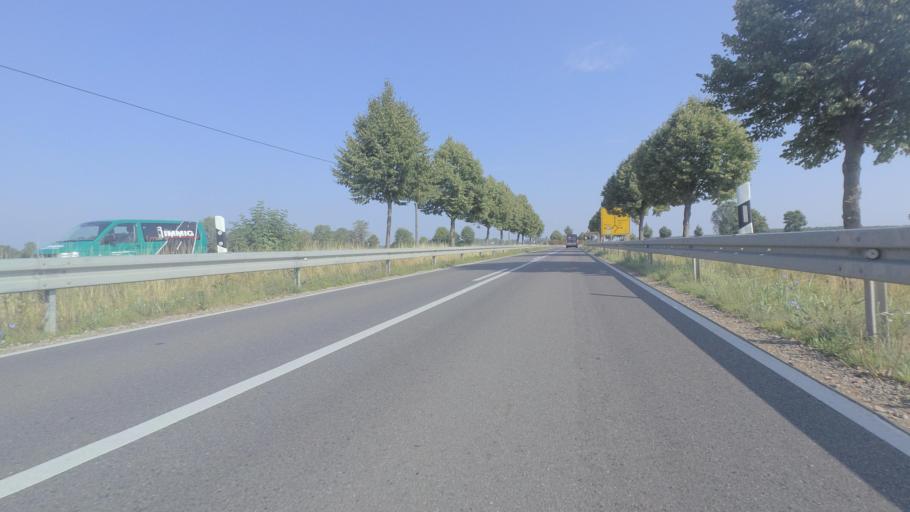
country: DE
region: Mecklenburg-Vorpommern
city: Malchow
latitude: 53.5173
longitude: 12.4231
